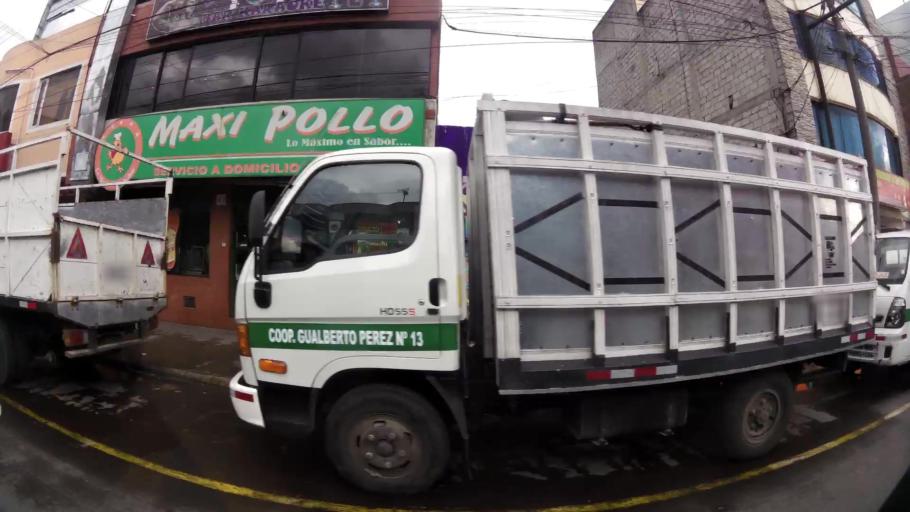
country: EC
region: Pichincha
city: Quito
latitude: -0.2573
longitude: -78.5422
